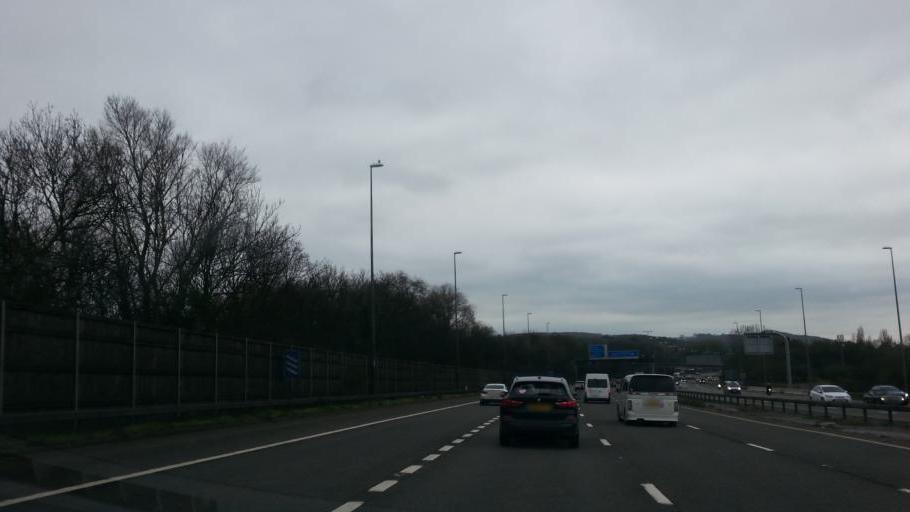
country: GB
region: England
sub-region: North Somerset
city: Easton-in-Gordano
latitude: 51.4817
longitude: -2.7008
